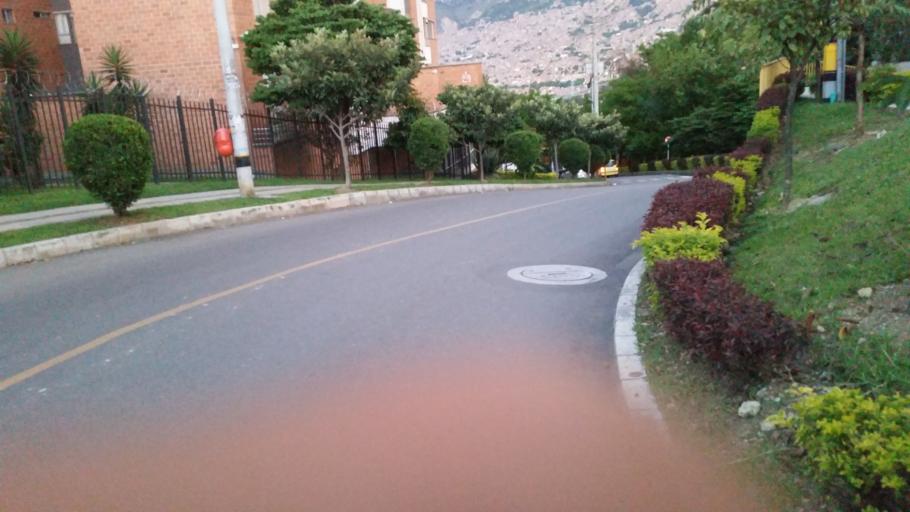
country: CO
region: Antioquia
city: Medellin
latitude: 6.2810
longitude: -75.5786
